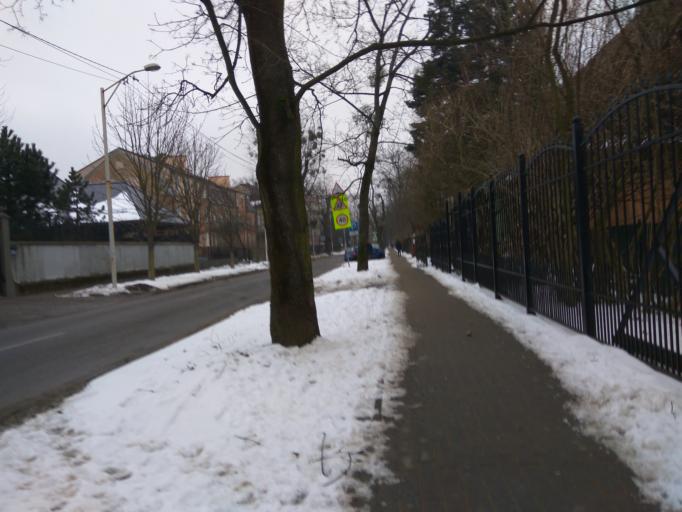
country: RU
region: Kaliningrad
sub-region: Gorod Kaliningrad
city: Kaliningrad
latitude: 54.7173
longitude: 20.4663
